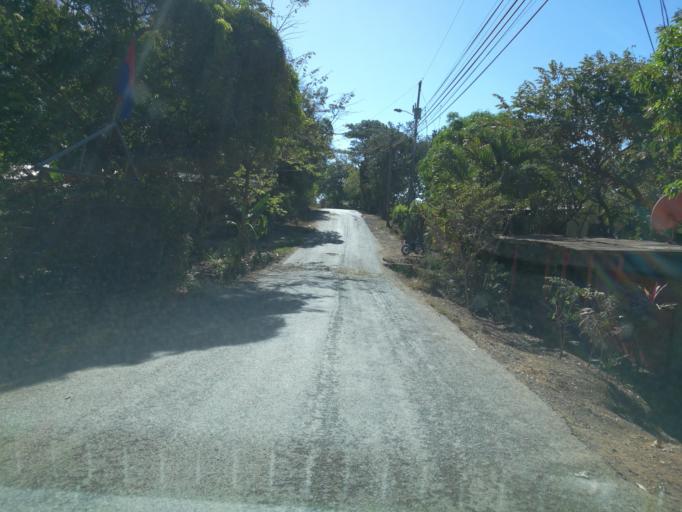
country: CR
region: Guanacaste
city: Juntas
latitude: 10.0962
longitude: -84.9833
